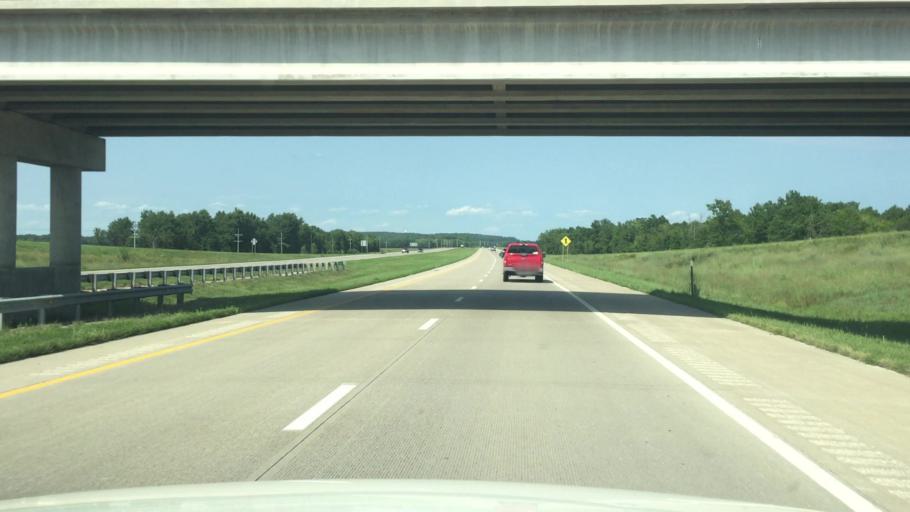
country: US
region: Kansas
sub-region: Linn County
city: Pleasanton
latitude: 38.2177
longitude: -94.7010
